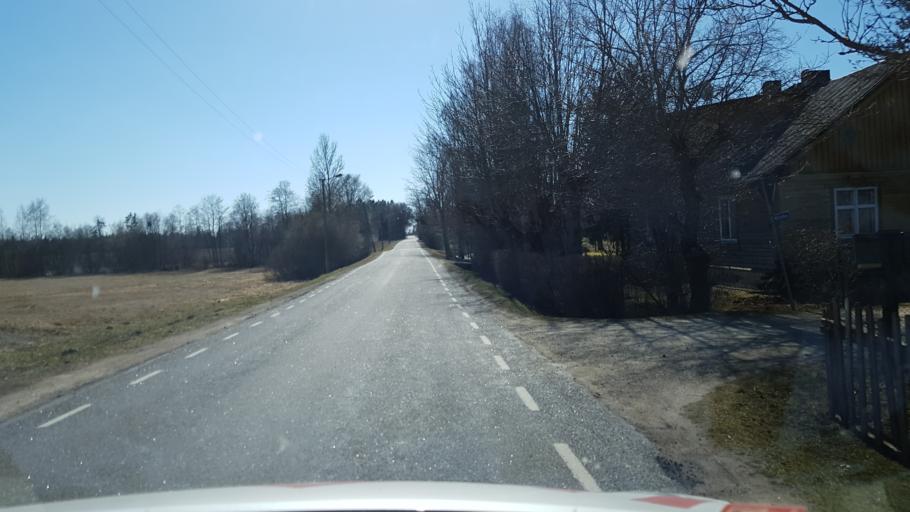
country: EE
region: Laeaene-Virumaa
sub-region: Tamsalu vald
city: Tamsalu
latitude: 59.0869
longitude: 26.1658
